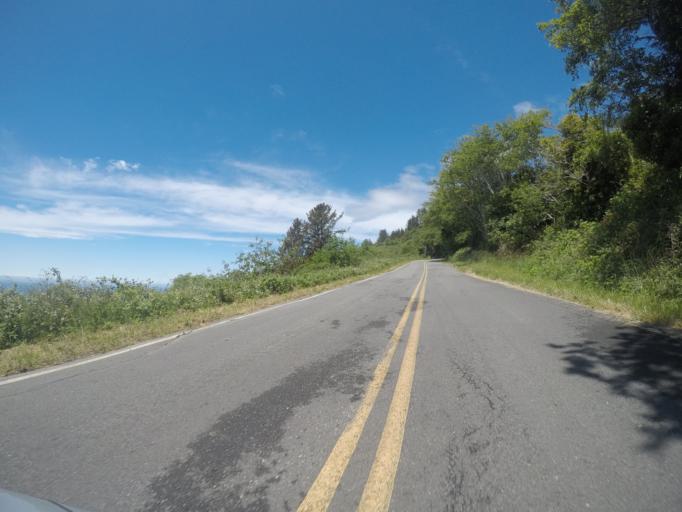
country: US
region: California
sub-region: Del Norte County
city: Bertsch-Oceanview
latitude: 41.5519
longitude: -124.0822
